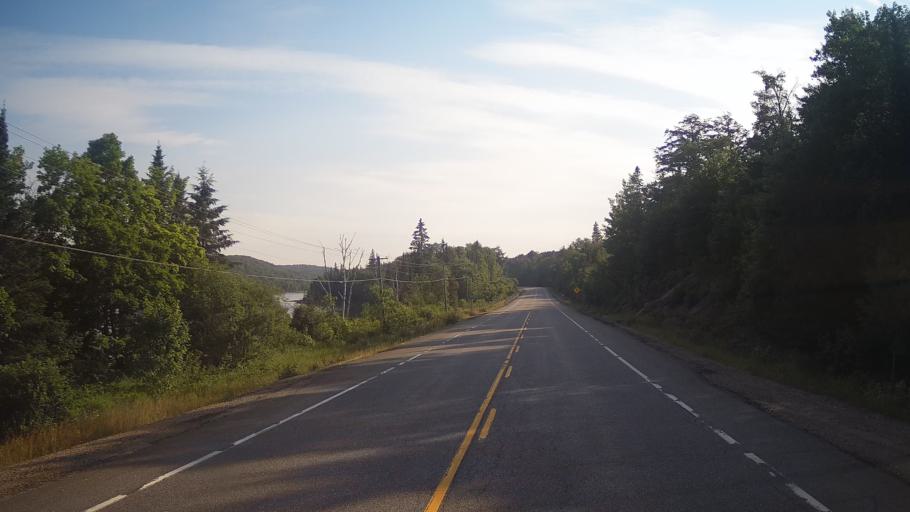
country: CA
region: Ontario
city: Huntsville
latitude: 45.4223
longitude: -78.8449
